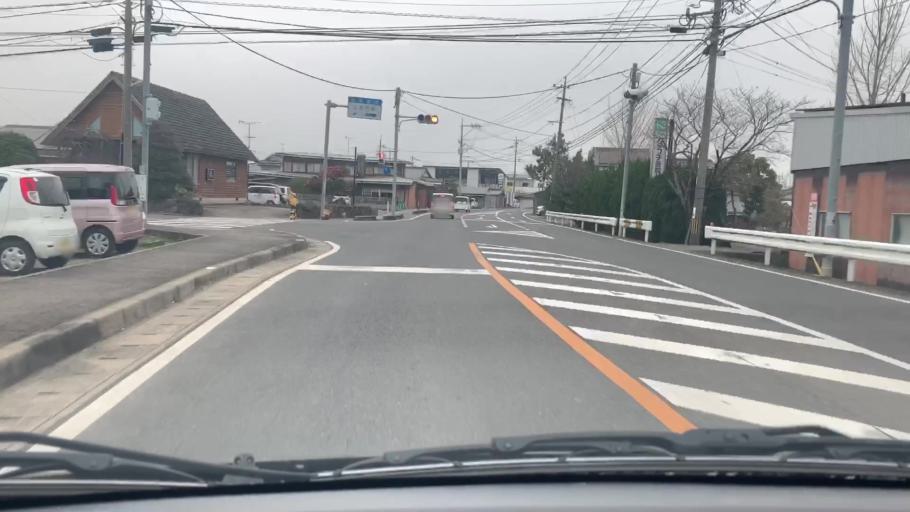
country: JP
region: Saga Prefecture
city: Saga-shi
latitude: 33.1952
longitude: 130.1929
